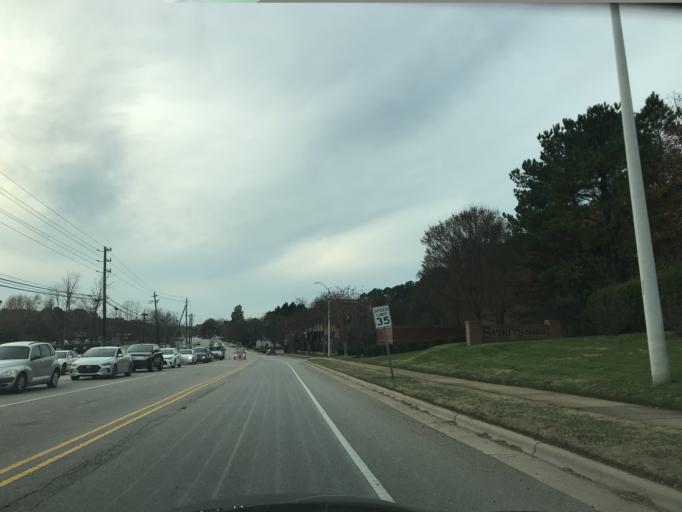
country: US
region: North Carolina
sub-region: Wake County
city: Cary
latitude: 35.7921
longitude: -78.7641
